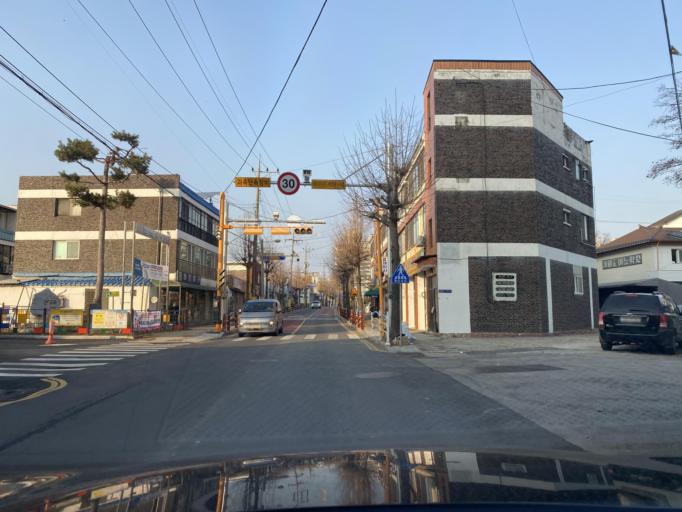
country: KR
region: Chungcheongnam-do
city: Yesan
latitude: 36.6833
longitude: 126.8326
